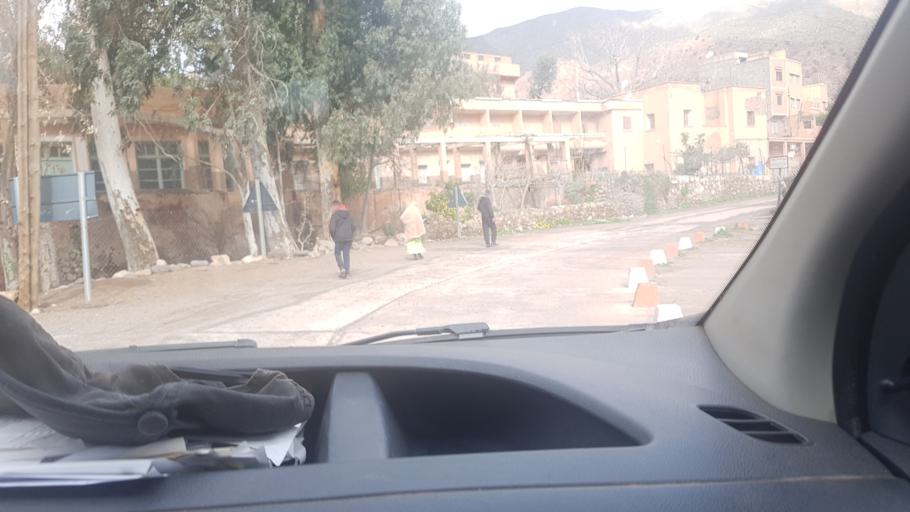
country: MA
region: Marrakech-Tensift-Al Haouz
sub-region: Al-Haouz
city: Azgour
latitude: 30.9983
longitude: -8.1577
